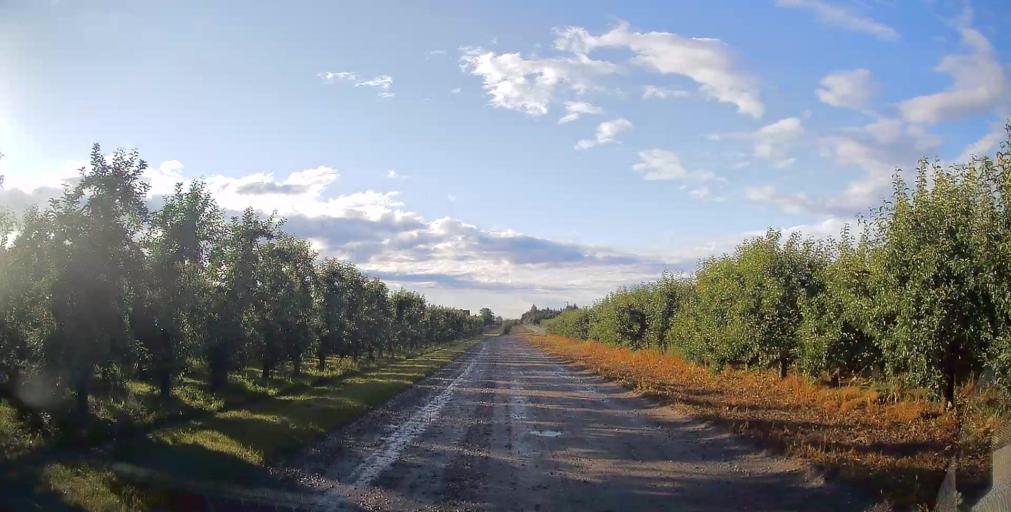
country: PL
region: Masovian Voivodeship
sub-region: Powiat grojecki
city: Goszczyn
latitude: 51.7476
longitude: 20.8865
